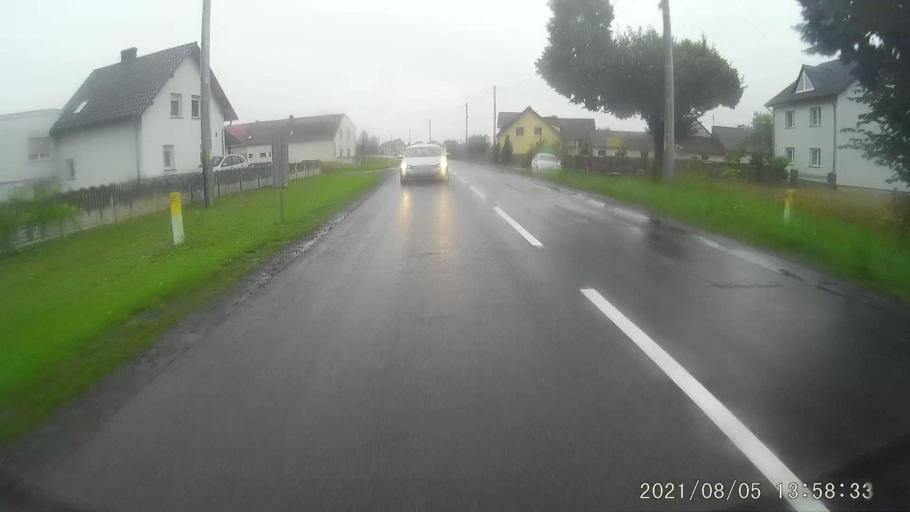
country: PL
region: Opole Voivodeship
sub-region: Powiat krapkowicki
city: Krapkowice
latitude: 50.4550
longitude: 17.9239
